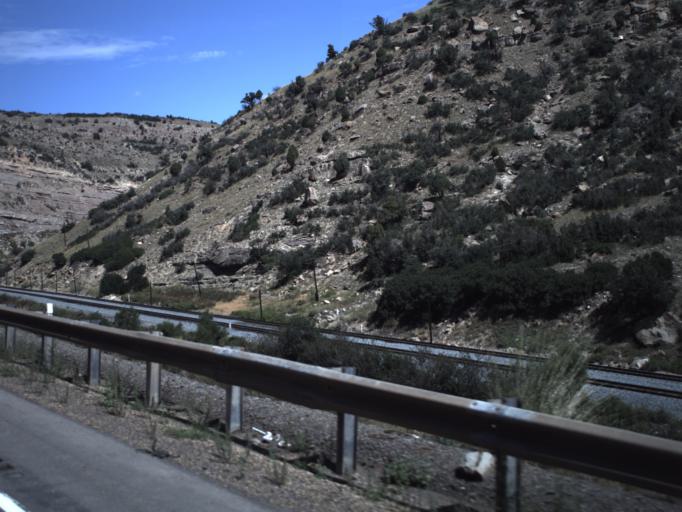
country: US
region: Utah
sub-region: Carbon County
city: Helper
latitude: 39.8028
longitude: -110.9398
